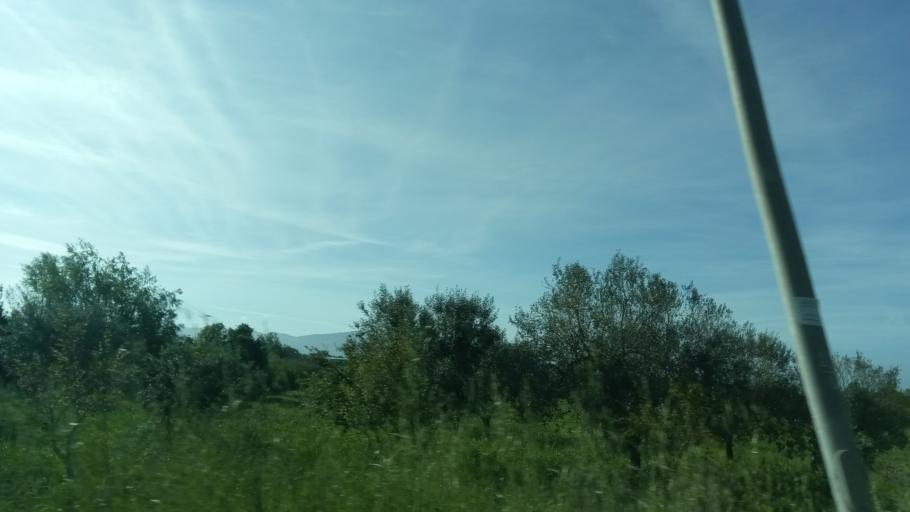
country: IT
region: Latium
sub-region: Provincia di Latina
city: Grunuovo-Campomaggiore San Luca
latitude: 41.2656
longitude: 13.7819
